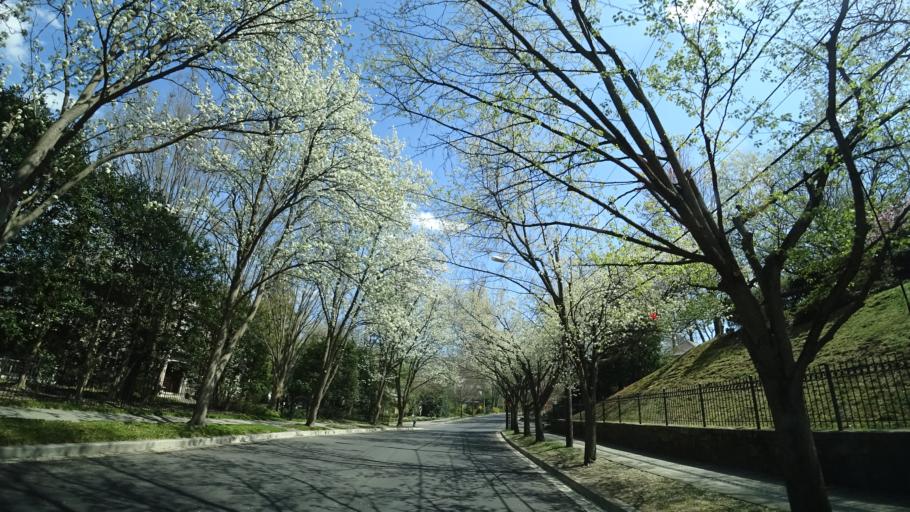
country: US
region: Maryland
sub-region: Montgomery County
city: Chevy Chase
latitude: 38.9511
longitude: -77.0585
